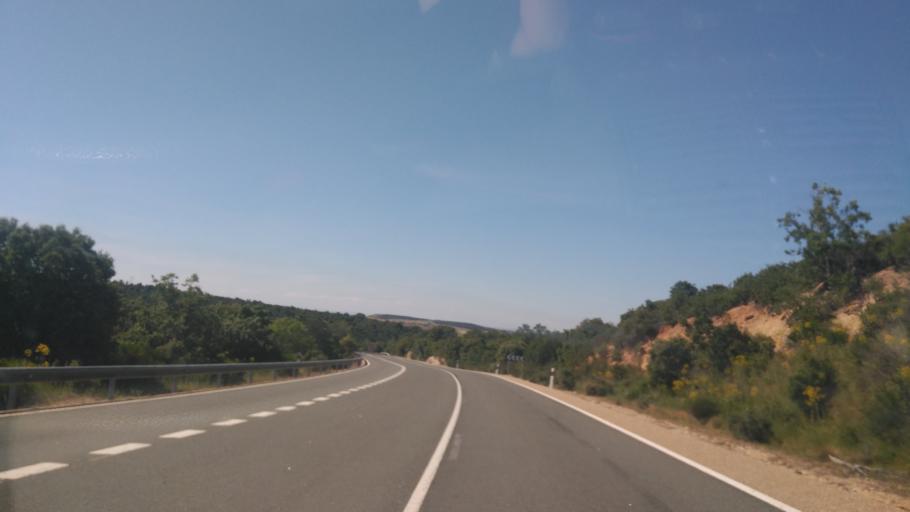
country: ES
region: Castille and Leon
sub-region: Provincia de Zamora
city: Corrales
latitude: 41.3002
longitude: -5.7251
